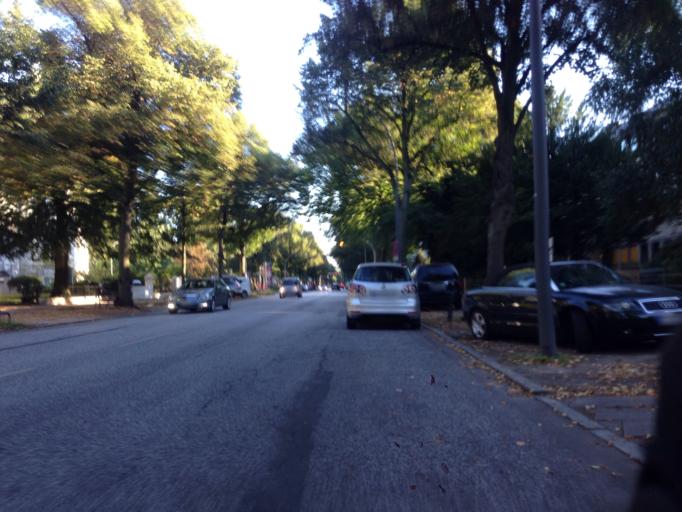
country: DE
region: Hamburg
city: Eimsbuettel
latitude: 53.5752
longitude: 9.9887
